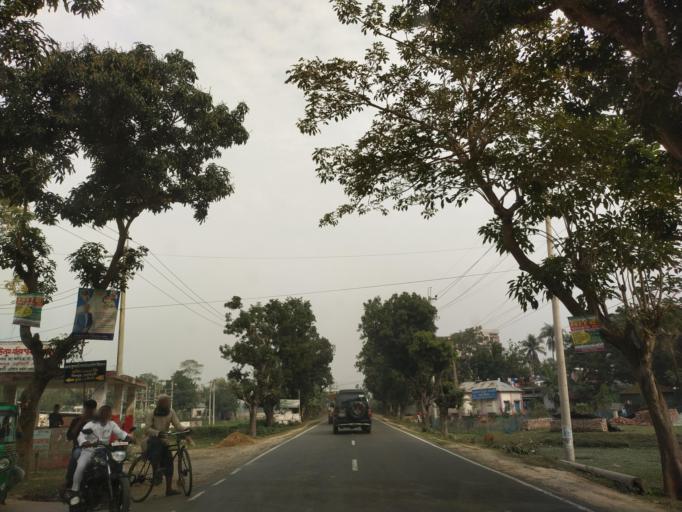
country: BD
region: Dhaka
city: Narsingdi
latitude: 23.9871
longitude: 90.7355
